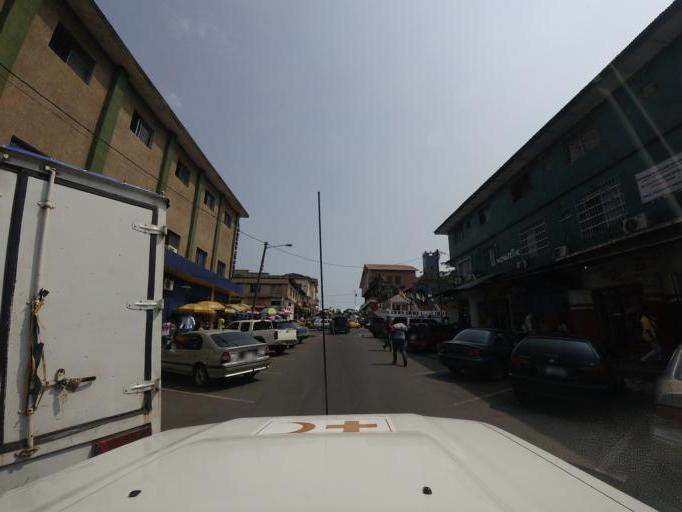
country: LR
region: Montserrado
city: Monrovia
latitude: 6.3163
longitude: -10.8049
